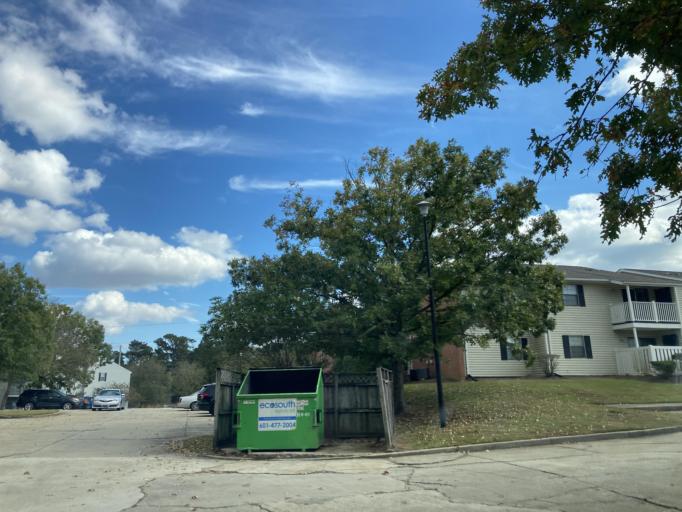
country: US
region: Mississippi
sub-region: Lamar County
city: Arnold Line
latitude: 31.3299
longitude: -89.3554
